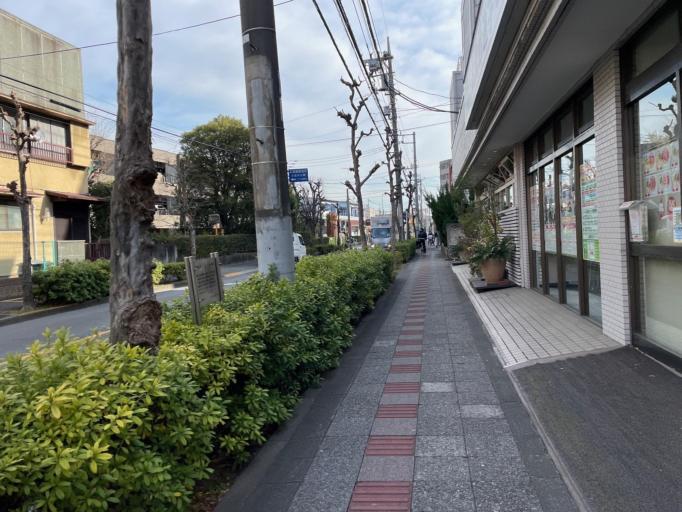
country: JP
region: Tokyo
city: Nishi-Tokyo-shi
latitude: 35.7055
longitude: 139.5124
